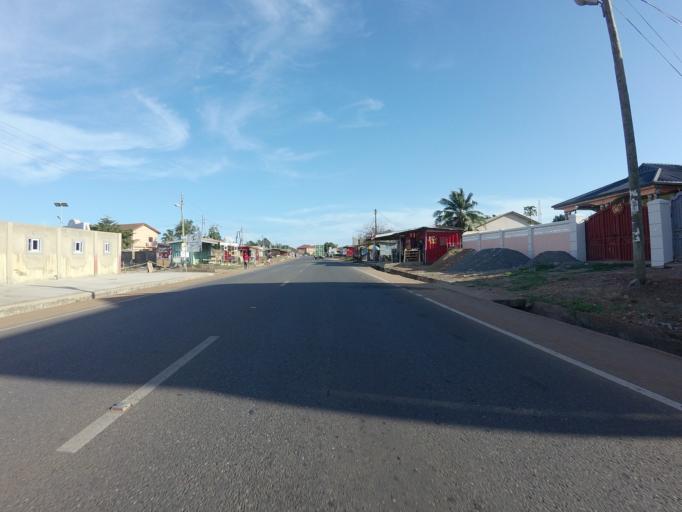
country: GH
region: Greater Accra
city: Nungua
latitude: 5.6363
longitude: -0.0916
